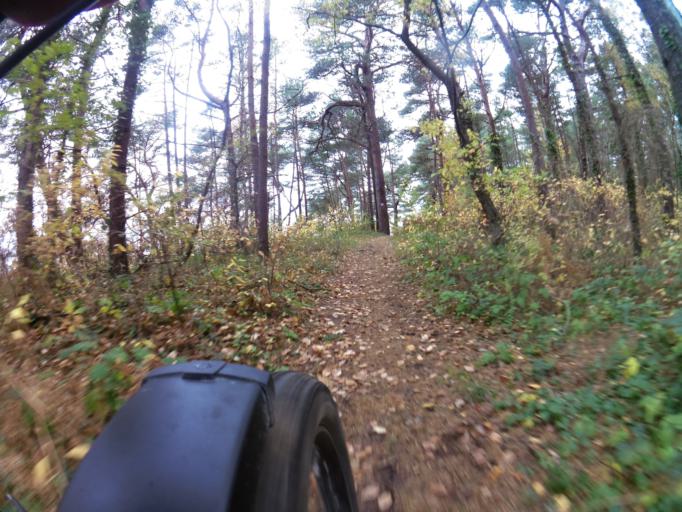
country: PL
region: Pomeranian Voivodeship
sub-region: Powiat pucki
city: Jastarnia
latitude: 54.6851
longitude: 18.7070
